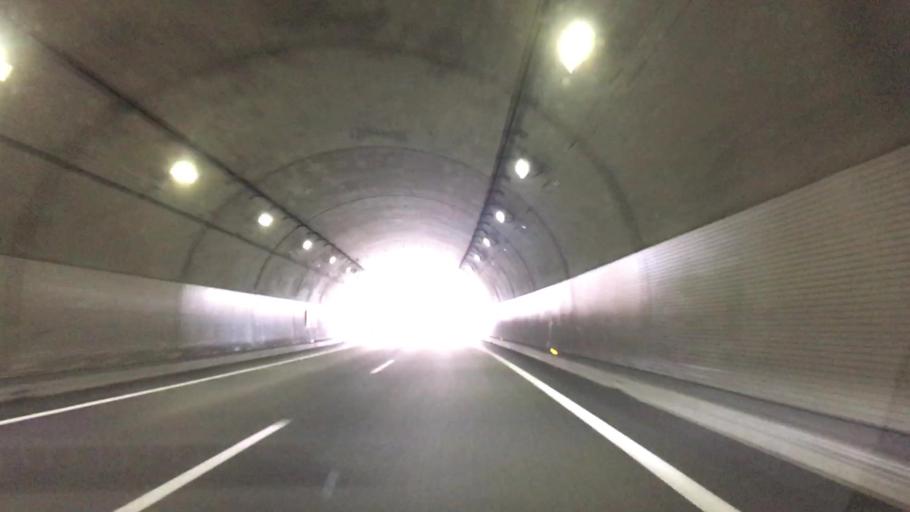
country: JP
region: Gifu
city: Tajimi
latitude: 35.2964
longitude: 137.1799
